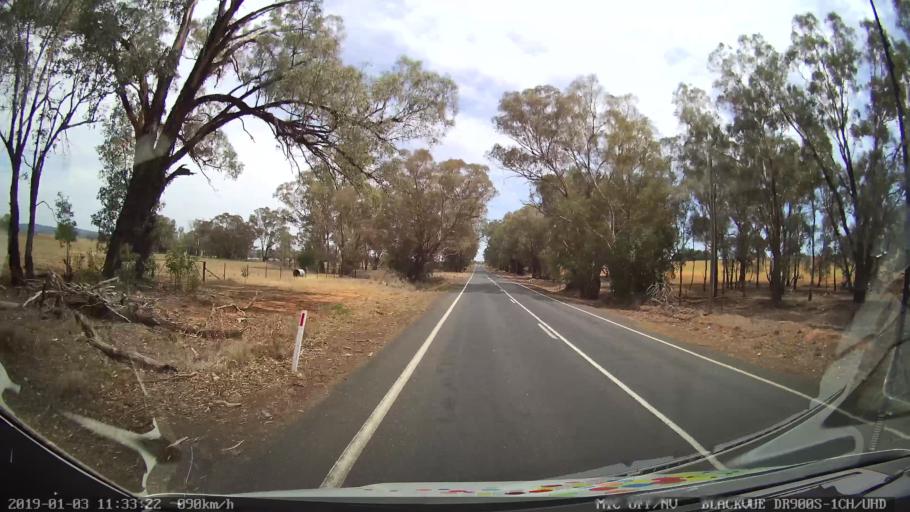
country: AU
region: New South Wales
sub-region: Weddin
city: Grenfell
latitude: -33.9476
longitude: 148.1713
